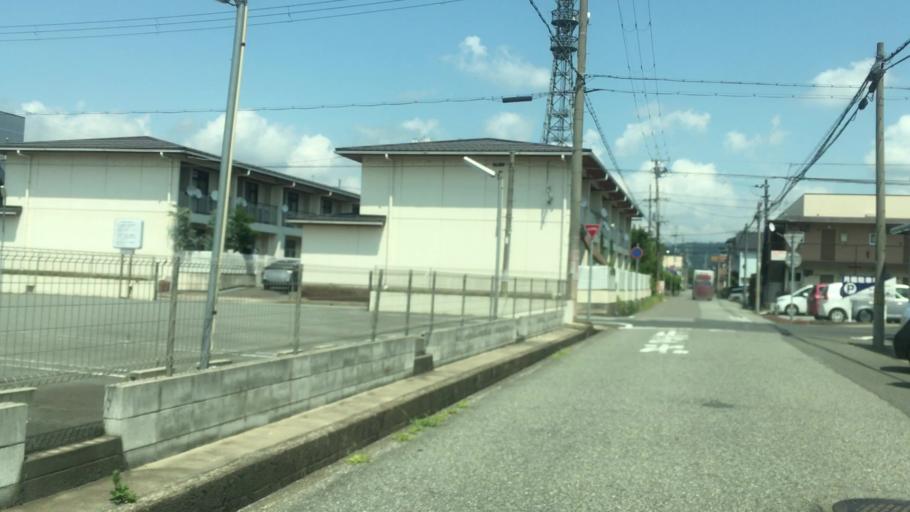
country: JP
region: Hyogo
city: Toyooka
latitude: 35.5481
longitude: 134.8194
